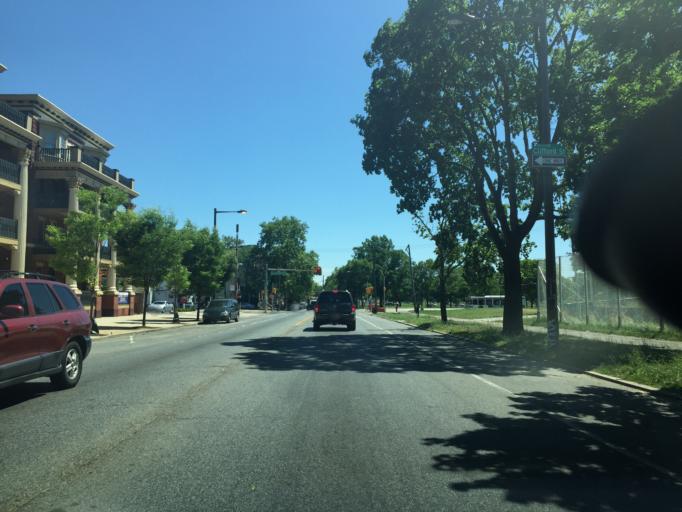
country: US
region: Pennsylvania
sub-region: Philadelphia County
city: Philadelphia
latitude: 39.9835
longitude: -75.1882
